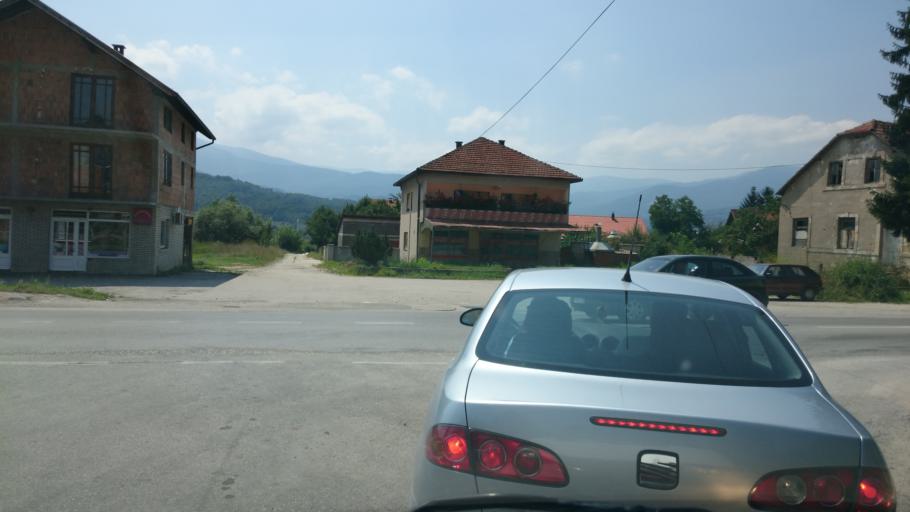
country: BA
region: Federation of Bosnia and Herzegovina
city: Vitez
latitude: 44.1504
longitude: 17.8121
